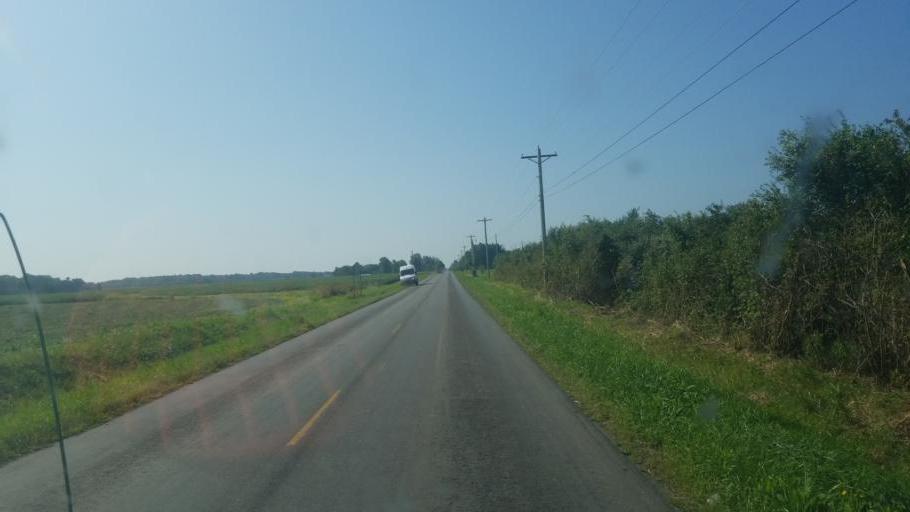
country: US
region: Ohio
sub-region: Wayne County
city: West Salem
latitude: 41.0265
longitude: -82.1636
